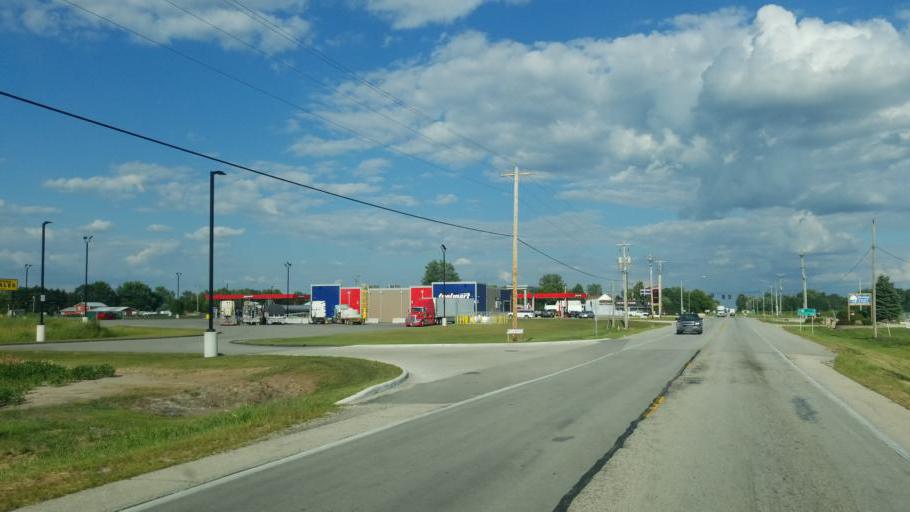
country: US
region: Ohio
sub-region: Wood County
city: Pemberville
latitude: 41.3413
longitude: -83.4199
